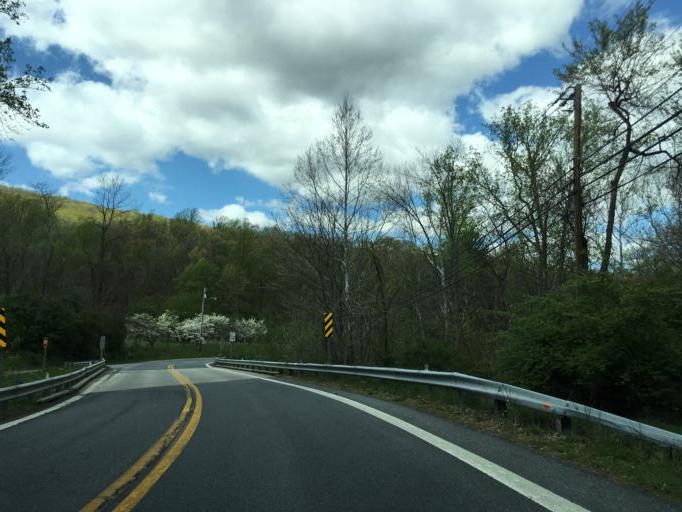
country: US
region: Maryland
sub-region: Frederick County
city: Thurmont
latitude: 39.6227
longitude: -77.4217
